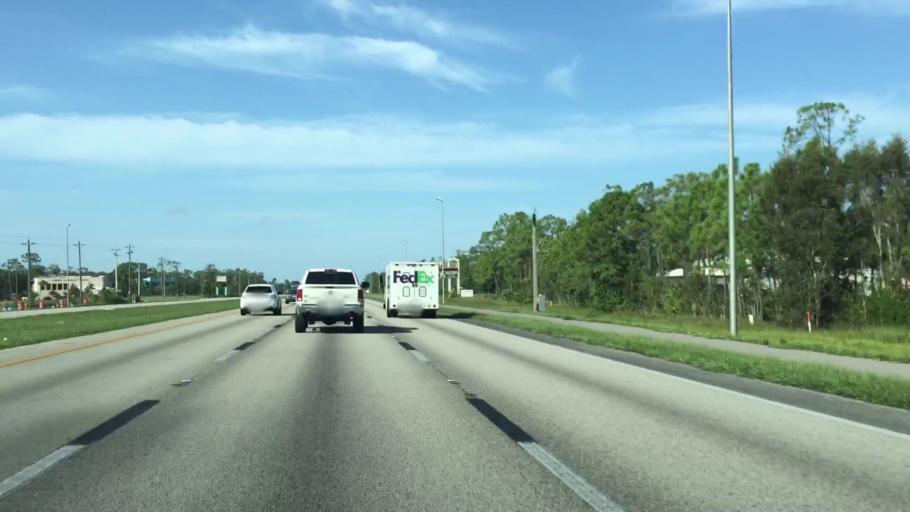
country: US
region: Florida
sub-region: Lee County
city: Fort Myers
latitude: 26.6047
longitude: -81.8249
